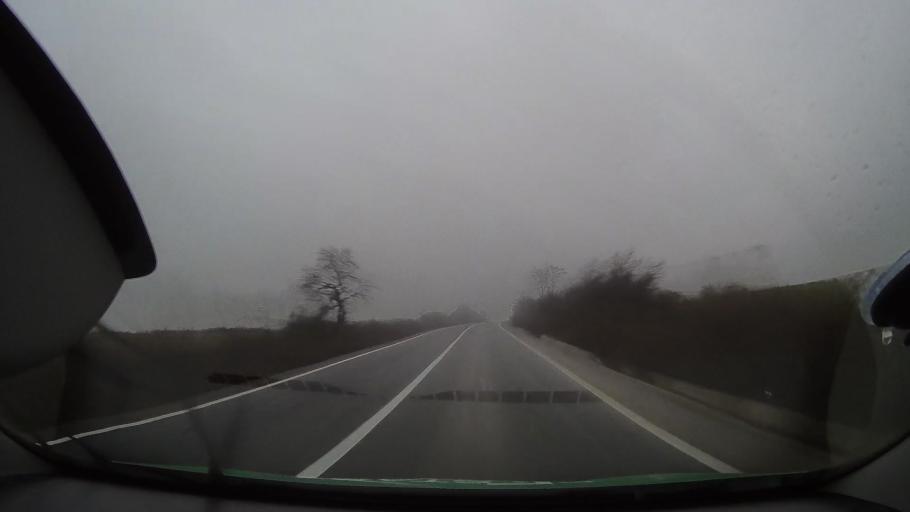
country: RO
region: Bihor
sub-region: Comuna Olcea
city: Calacea
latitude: 46.6459
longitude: 21.9572
